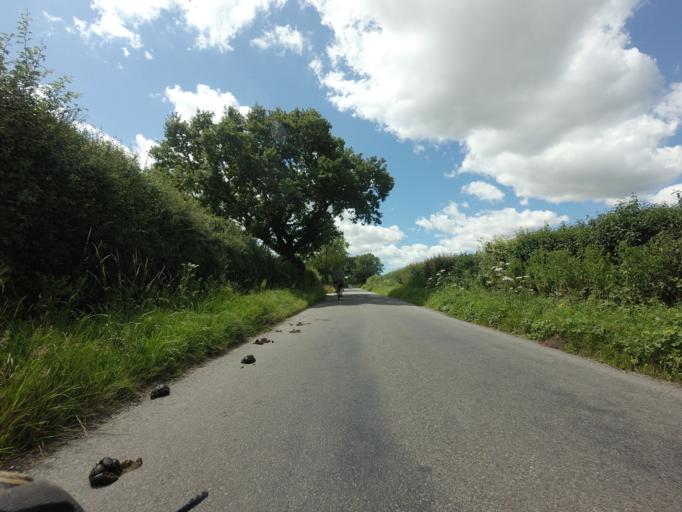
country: GB
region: England
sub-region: East Sussex
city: Ringmer
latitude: 50.8669
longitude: 0.1414
